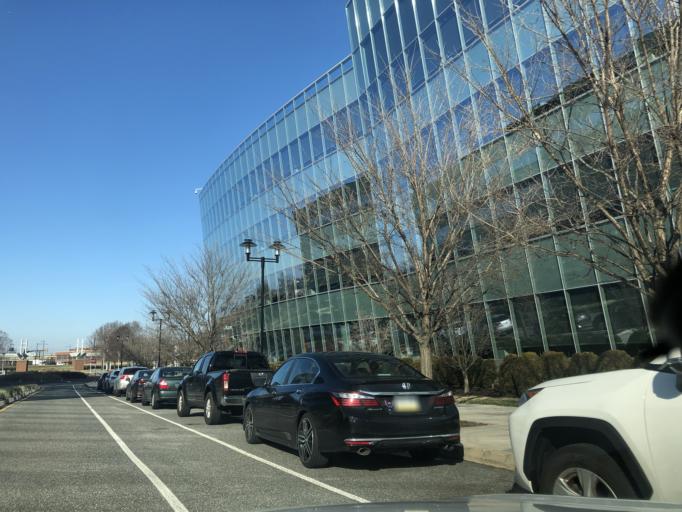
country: US
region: New Jersey
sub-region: Gloucester County
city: National Park
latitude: 39.8958
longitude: -75.1731
